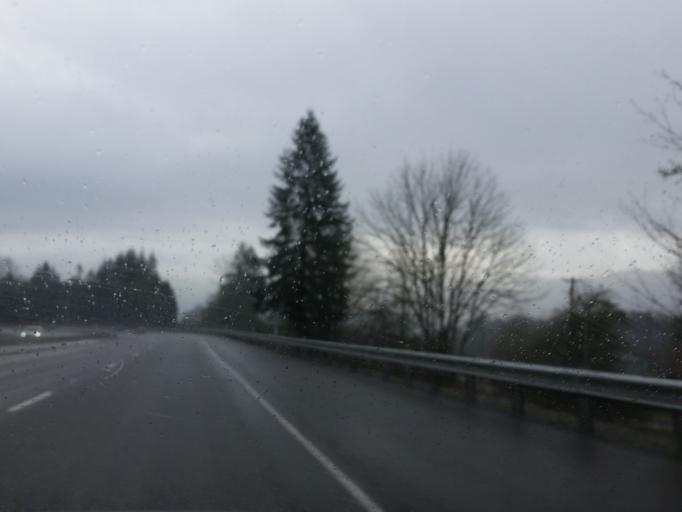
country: US
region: Washington
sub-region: Snohomish County
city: Cathcart
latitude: 47.8298
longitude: -122.0362
